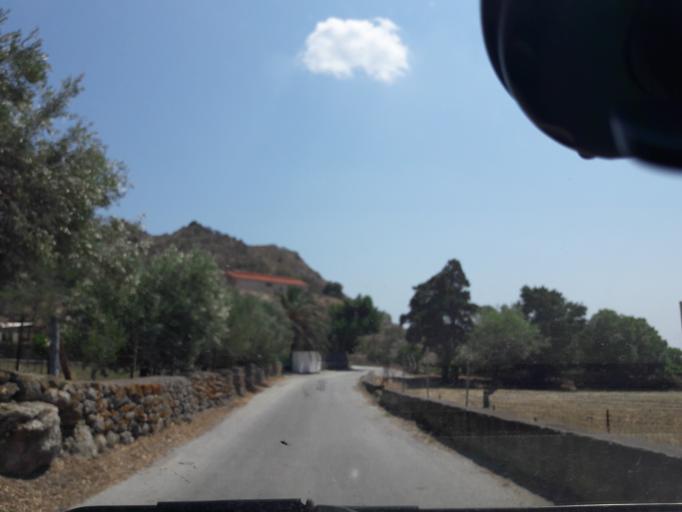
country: GR
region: North Aegean
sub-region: Nomos Lesvou
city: Myrina
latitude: 39.8476
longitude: 25.0850
